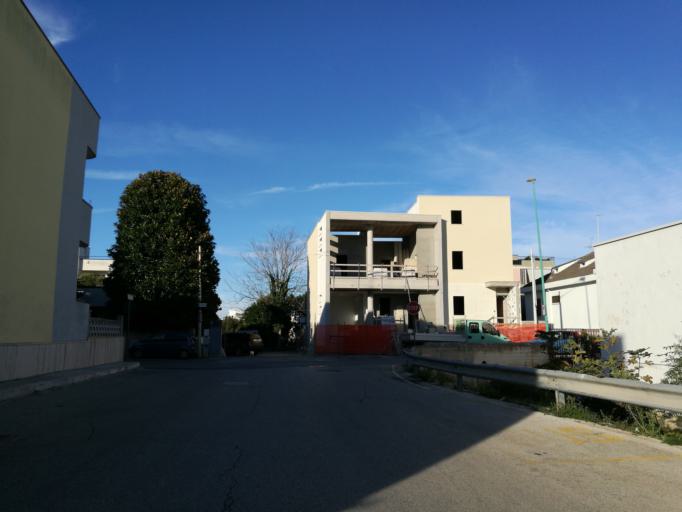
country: IT
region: Apulia
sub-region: Provincia di Bari
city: Adelfia
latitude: 41.0042
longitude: 16.8629
